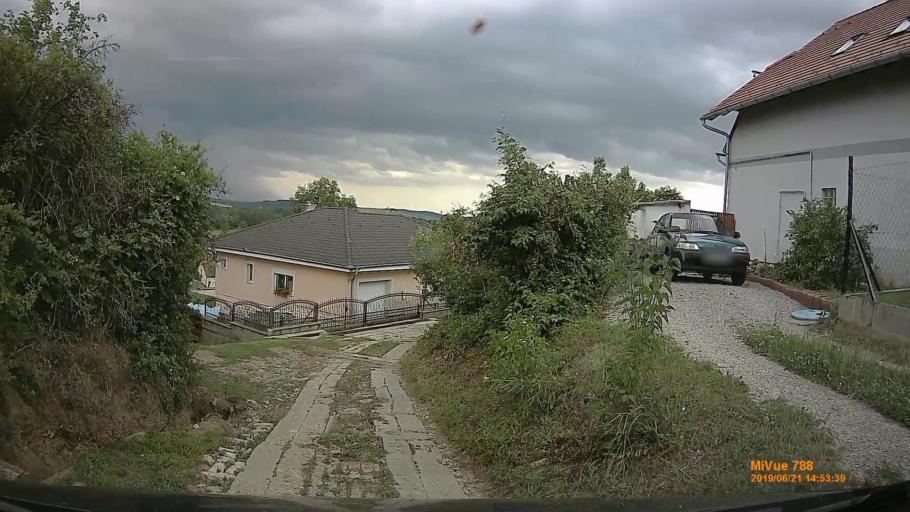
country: HU
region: Baranya
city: Hosszuheteny
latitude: 46.1278
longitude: 18.3108
